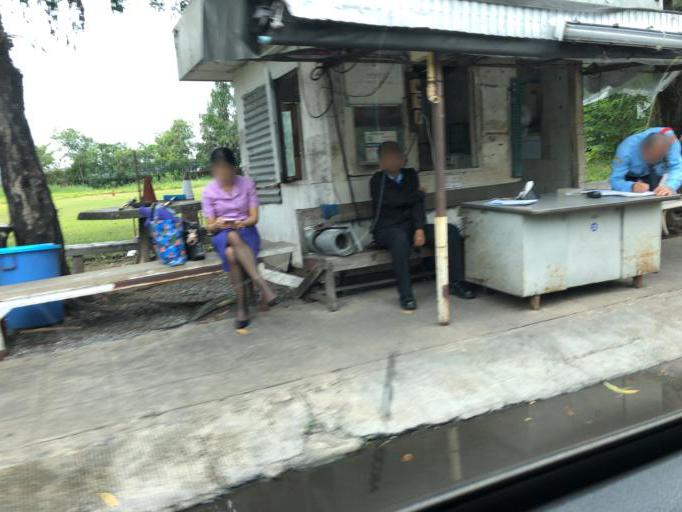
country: TH
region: Bangkok
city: Don Mueang
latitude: 13.9329
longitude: 100.6117
